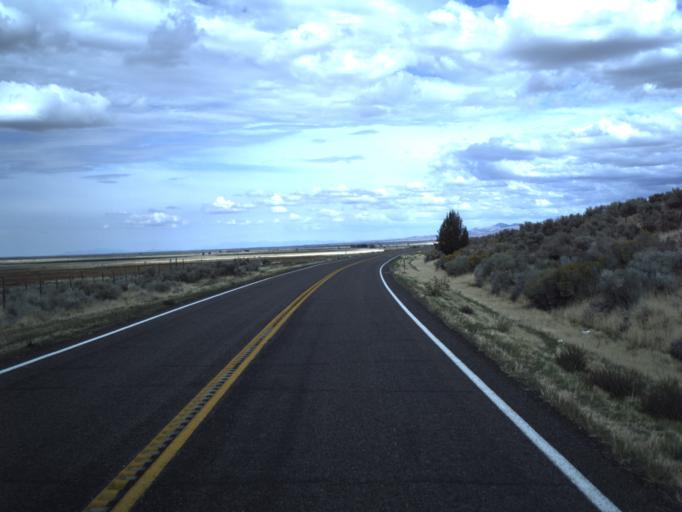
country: US
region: Utah
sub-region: Millard County
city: Fillmore
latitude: 38.9985
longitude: -112.4132
